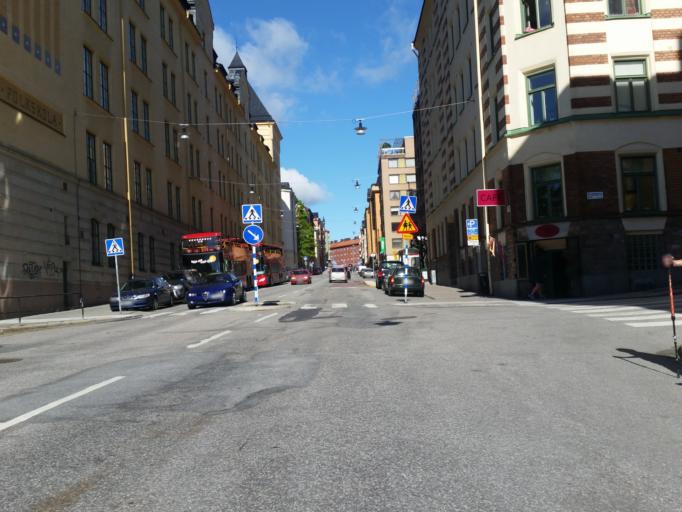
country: SE
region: Stockholm
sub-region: Stockholms Kommun
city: OEstermalm
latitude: 59.3132
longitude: 18.0948
